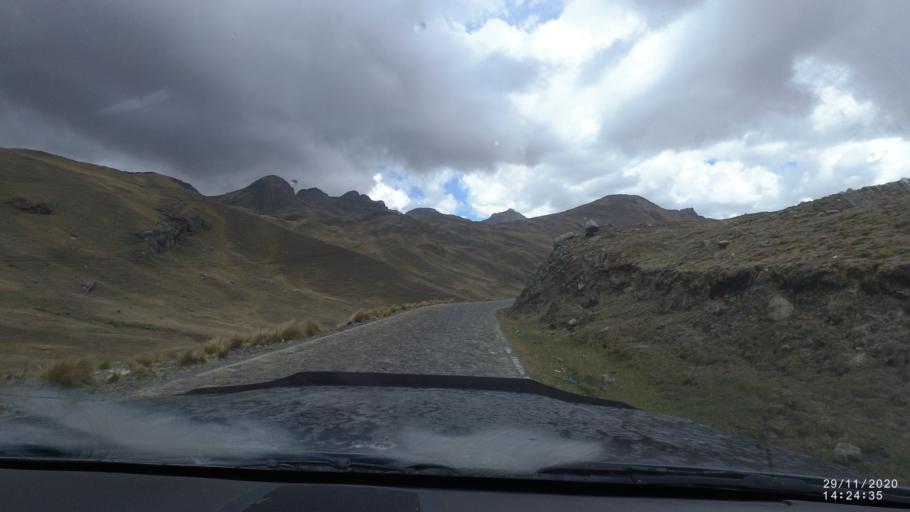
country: BO
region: Cochabamba
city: Sipe Sipe
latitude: -17.2543
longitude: -66.3782
